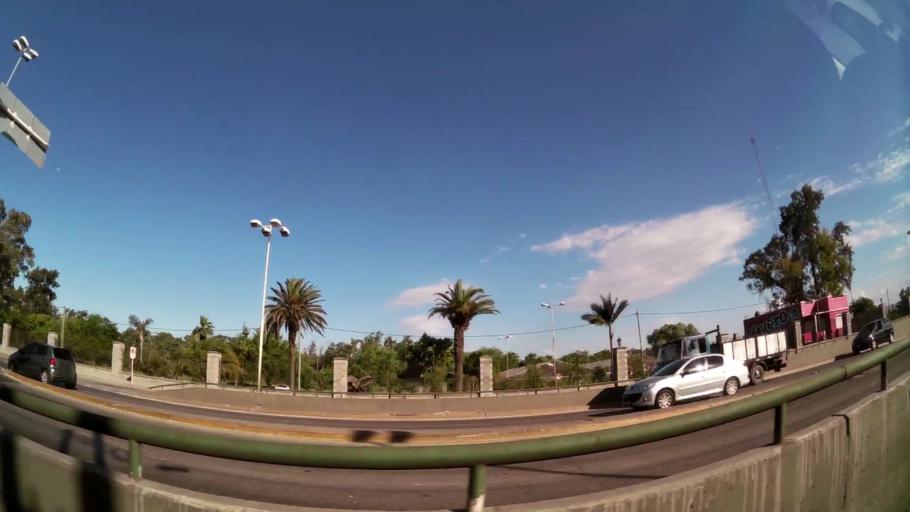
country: AR
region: Buenos Aires
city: Santa Catalina - Dique Lujan
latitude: -34.4932
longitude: -58.7039
